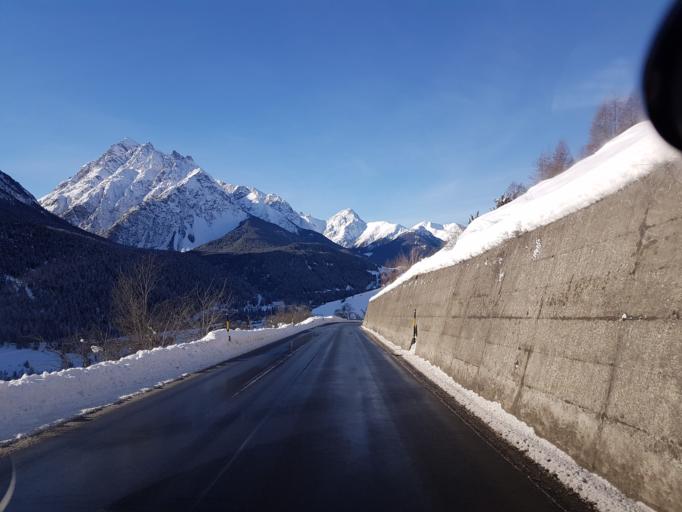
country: CH
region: Grisons
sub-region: Inn District
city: Scuol
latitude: 46.8060
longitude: 10.3160
